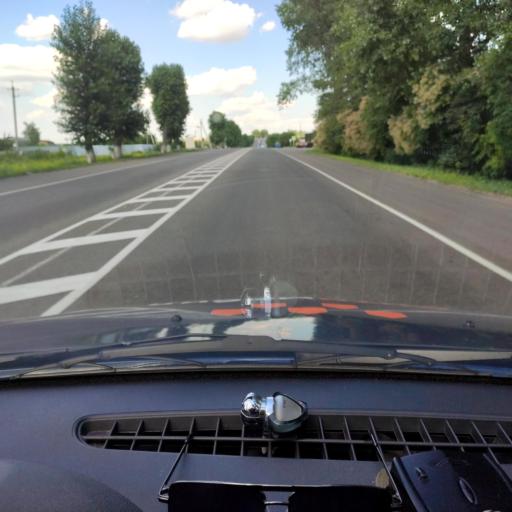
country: RU
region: Voronezj
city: Novovoronezh
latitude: 51.3362
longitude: 39.2657
